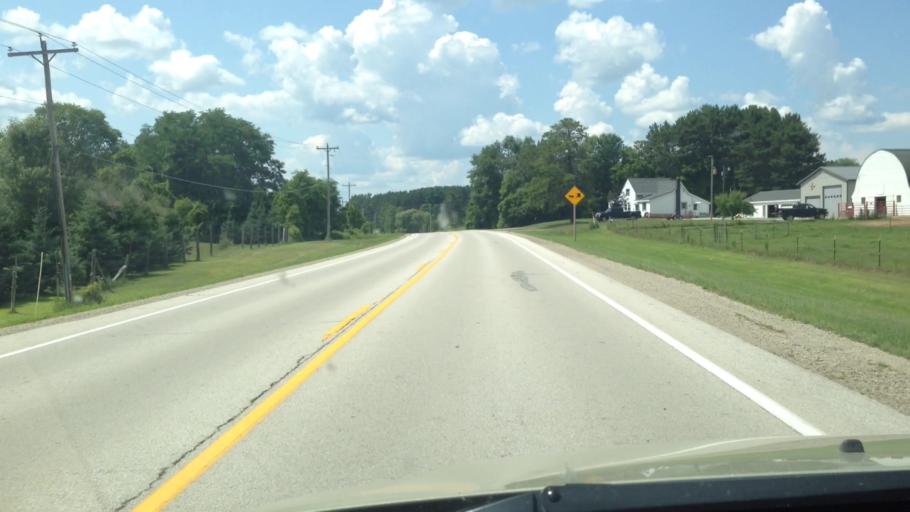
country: US
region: Wisconsin
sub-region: Brown County
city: Suamico
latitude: 44.6458
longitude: -88.0968
